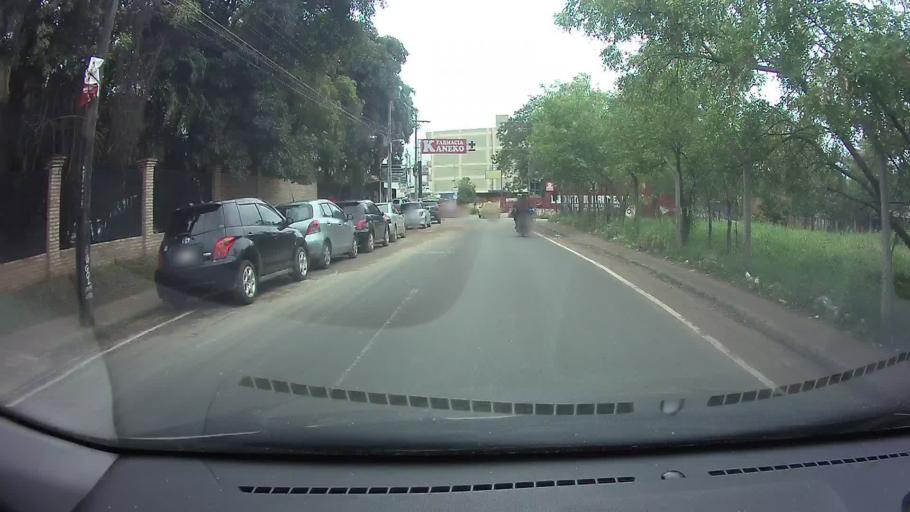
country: PY
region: Central
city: San Lorenzo
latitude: -25.3365
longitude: -57.5092
